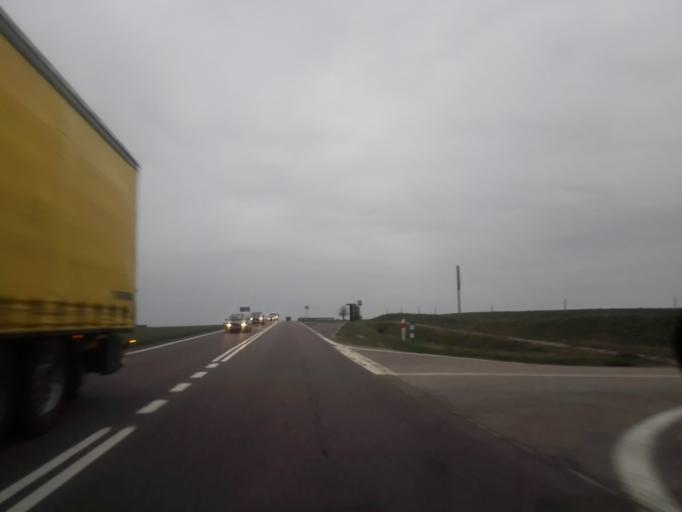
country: PL
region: Podlasie
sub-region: Powiat grajewski
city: Szczuczyn
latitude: 53.5119
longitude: 22.2430
